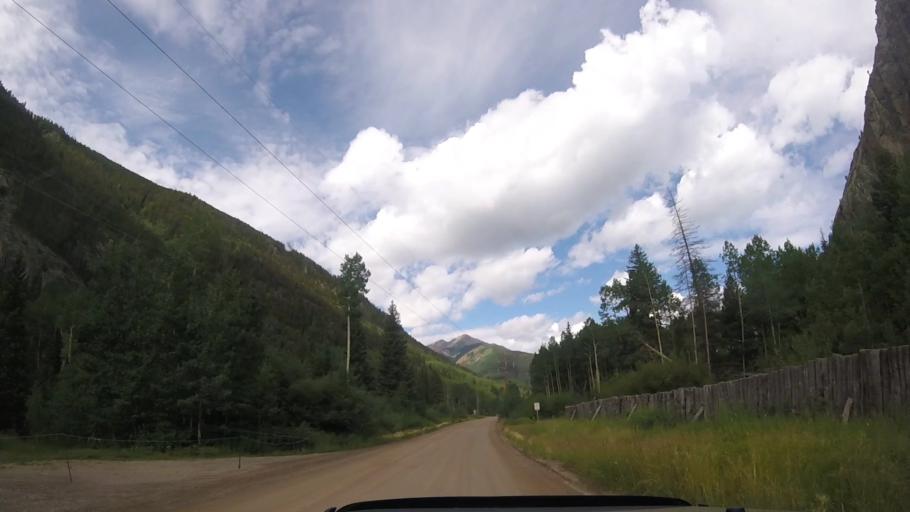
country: US
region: Colorado
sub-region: San Miguel County
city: Mountain Village
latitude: 37.8590
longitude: -107.8651
